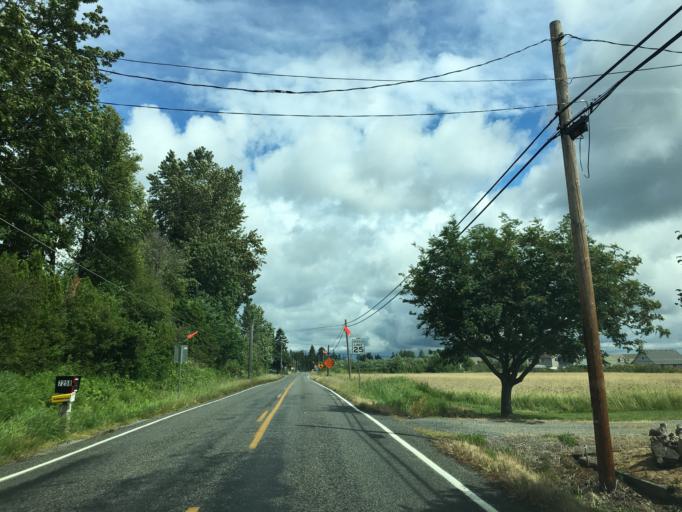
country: US
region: Washington
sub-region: Whatcom County
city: Birch Bay
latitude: 48.9052
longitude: -122.7487
